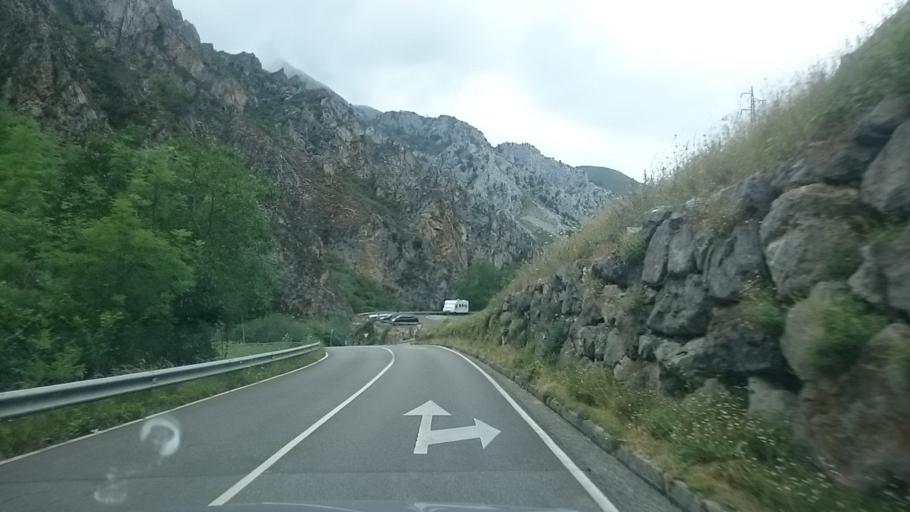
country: ES
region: Asturias
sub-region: Province of Asturias
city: Carrena
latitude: 43.2609
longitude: -4.8311
